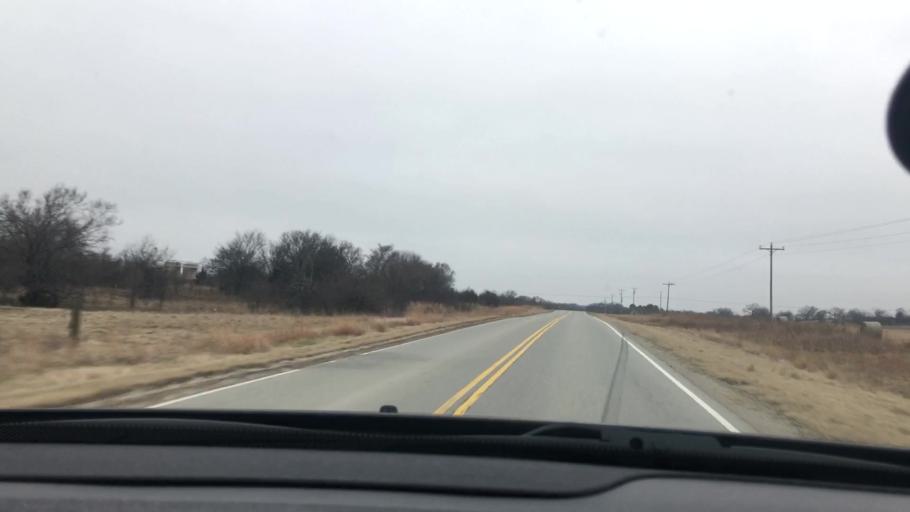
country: US
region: Oklahoma
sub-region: Coal County
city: Coalgate
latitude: 34.5109
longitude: -96.2926
